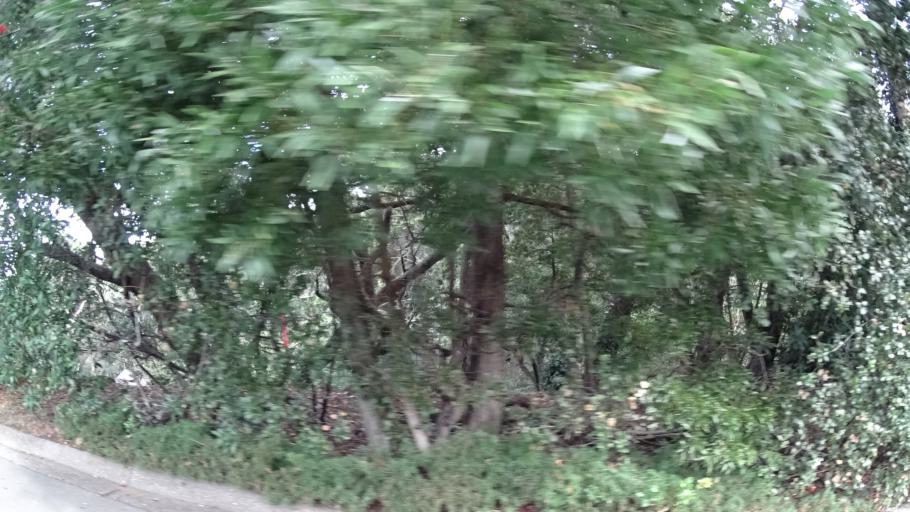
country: US
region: California
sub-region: San Mateo County
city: Hillsborough
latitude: 37.5680
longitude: -122.3901
